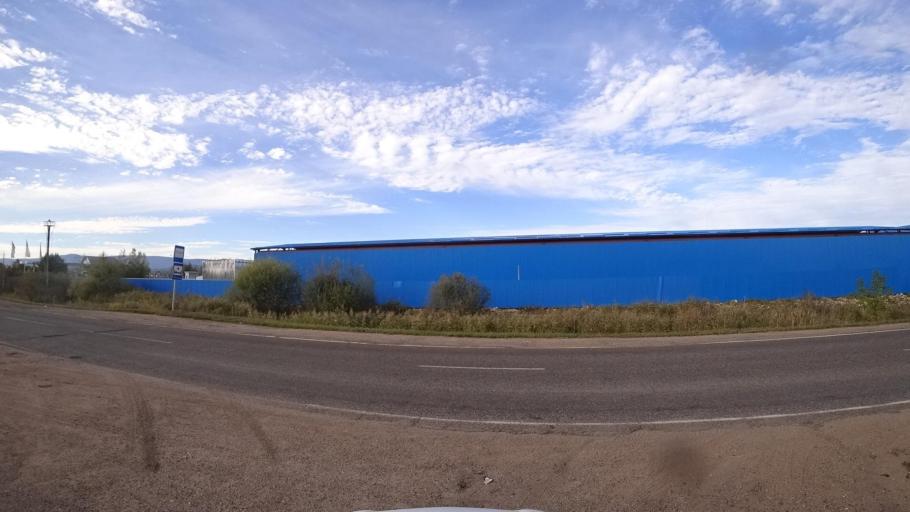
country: RU
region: Primorskiy
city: Dostoyevka
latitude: 44.2945
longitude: 133.4297
